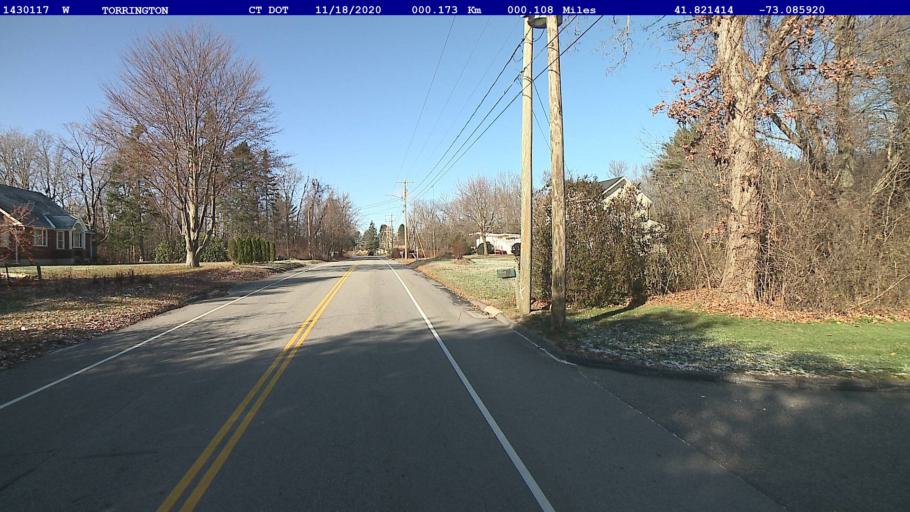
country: US
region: Connecticut
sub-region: Litchfield County
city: Torrington
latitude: 41.8214
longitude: -73.0859
